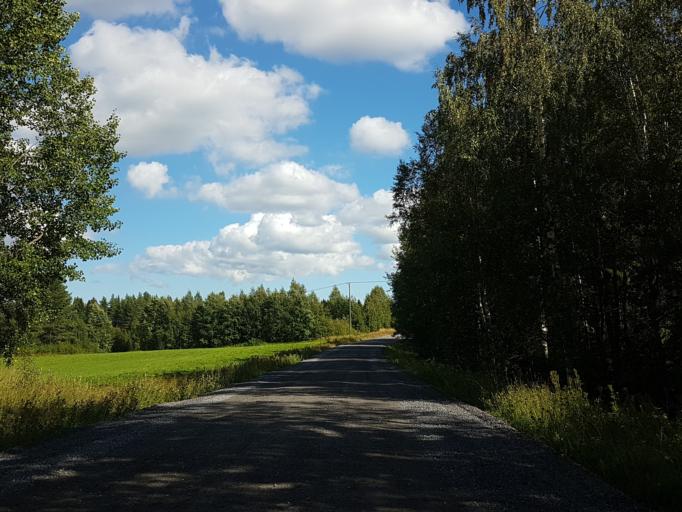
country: SE
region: Vaesterbotten
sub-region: Skelleftea Kommun
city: Burtraesk
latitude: 64.2942
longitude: 20.5172
